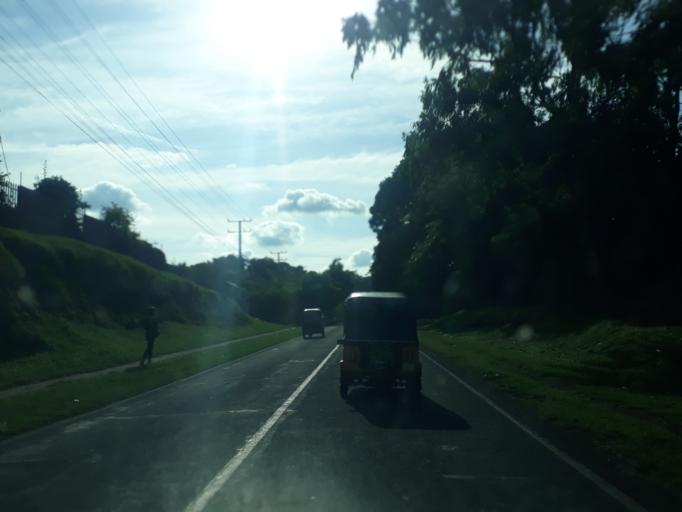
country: NI
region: Masaya
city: Masatepe
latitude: 11.9045
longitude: -86.1567
